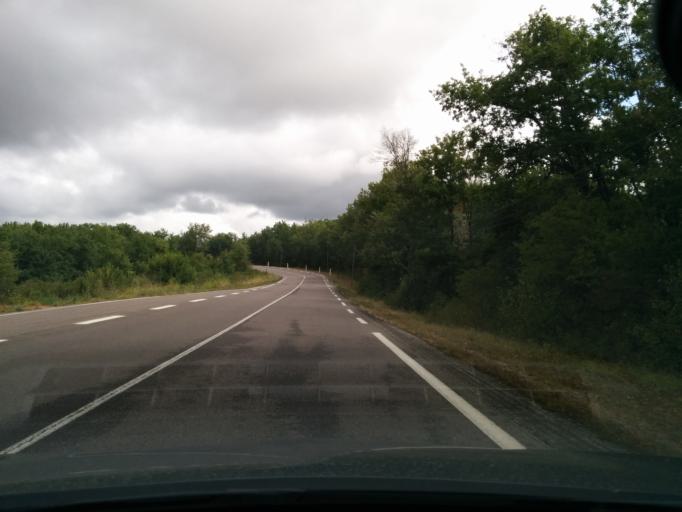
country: FR
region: Midi-Pyrenees
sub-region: Departement du Lot
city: Souillac
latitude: 44.9752
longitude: 1.5076
